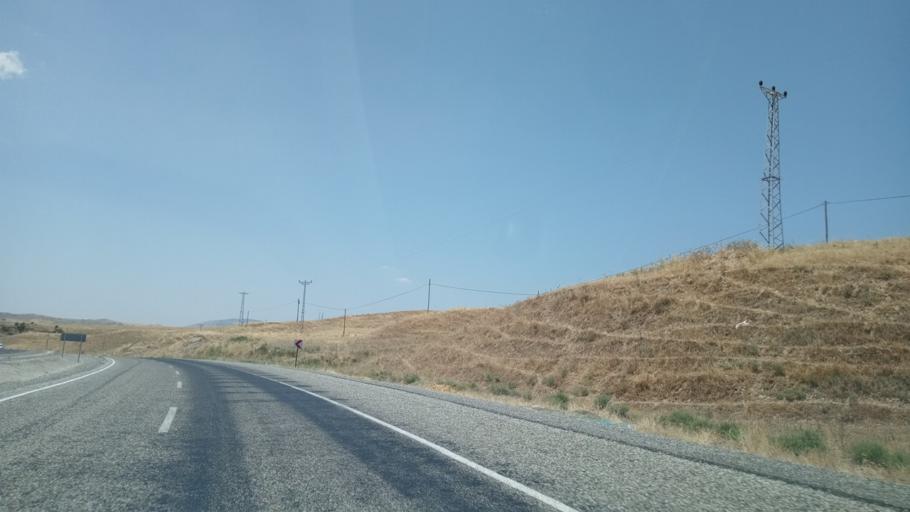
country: TR
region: Batman
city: Bekirhan
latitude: 38.1564
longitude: 41.3264
